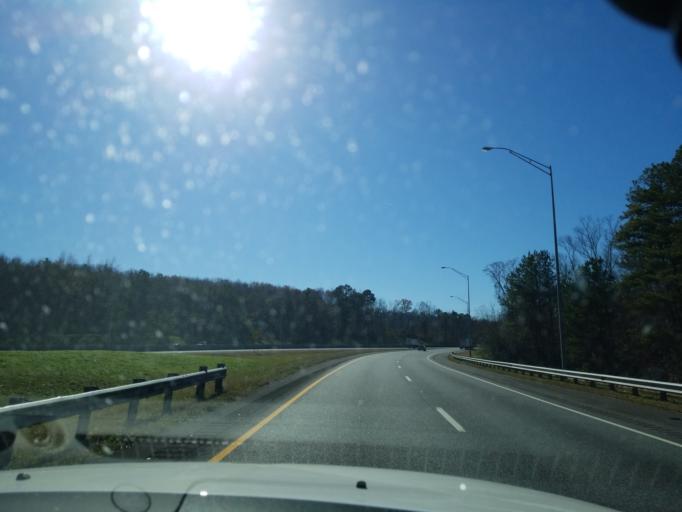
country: US
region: Alabama
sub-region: Jefferson County
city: Bessemer
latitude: 33.3370
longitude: -87.0347
